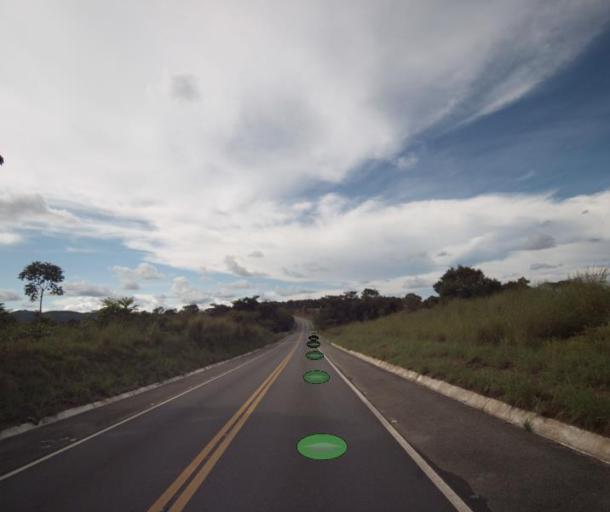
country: BR
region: Goias
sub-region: Barro Alto
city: Barro Alto
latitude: -15.1690
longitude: -48.7024
